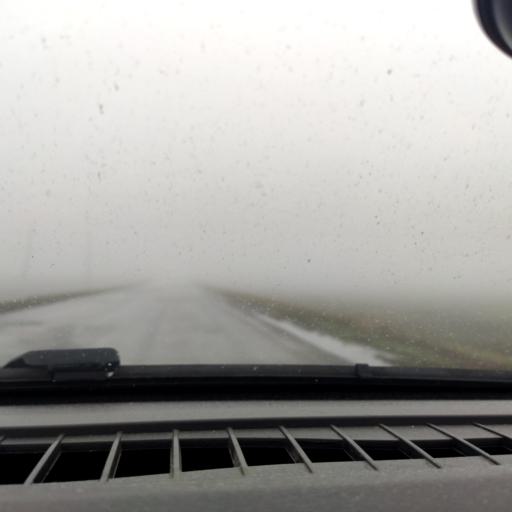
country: RU
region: Belgorod
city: Ilovka
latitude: 50.7183
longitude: 38.6754
